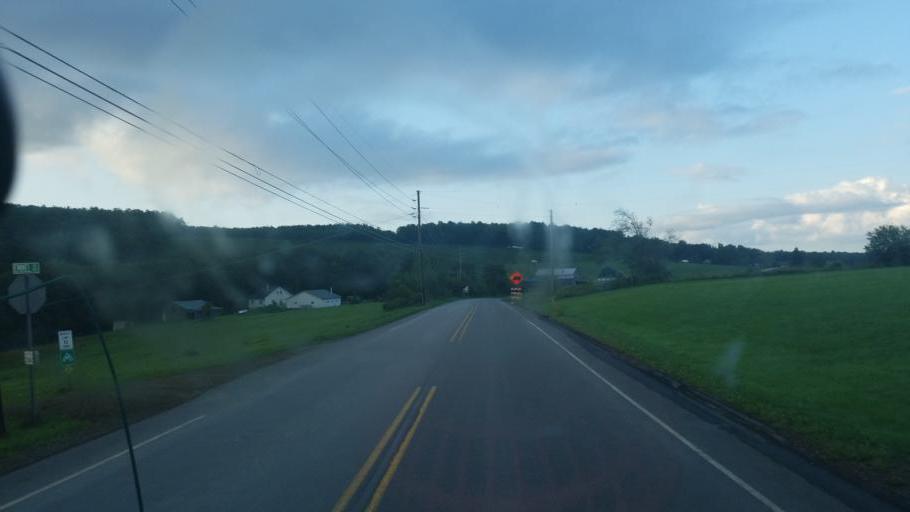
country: US
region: Pennsylvania
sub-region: Potter County
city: Galeton
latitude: 41.8579
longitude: -77.7669
